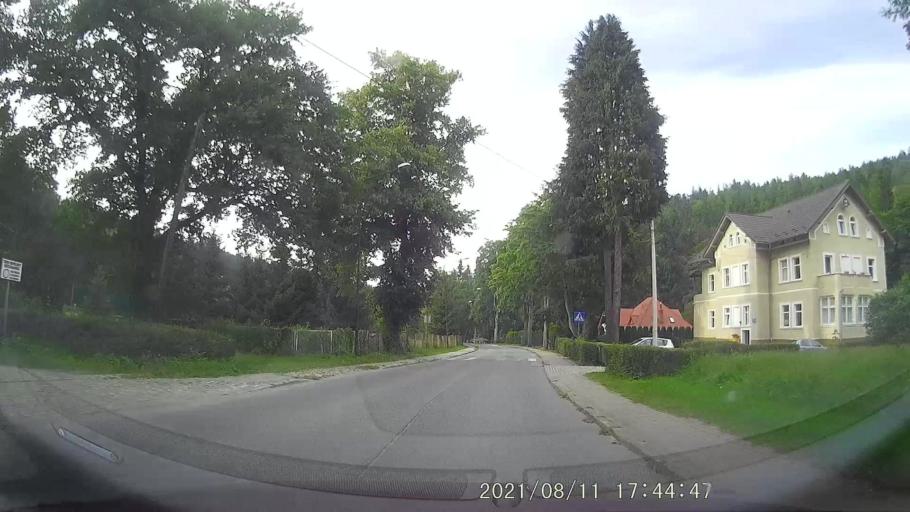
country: PL
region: Lower Silesian Voivodeship
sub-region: Powiat klodzki
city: Duszniki-Zdroj
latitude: 50.3873
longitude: 16.3838
